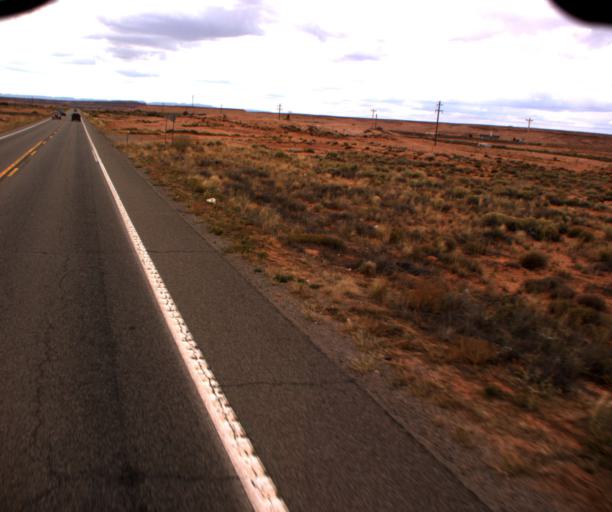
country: US
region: Arizona
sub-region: Navajo County
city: Kayenta
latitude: 36.8329
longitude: -109.8551
